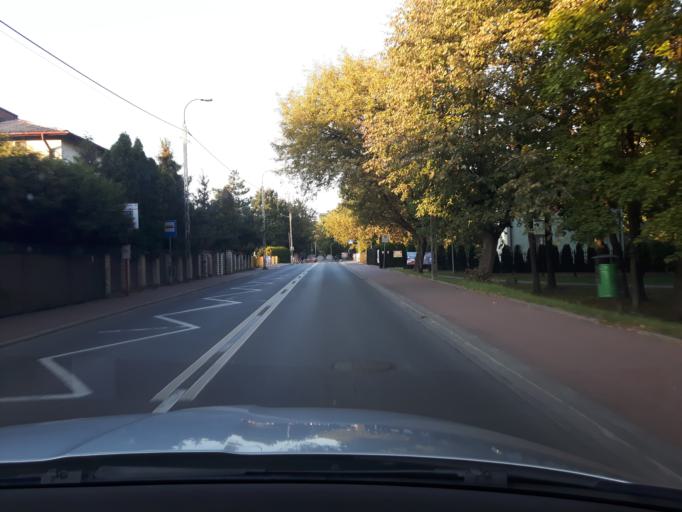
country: PL
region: Masovian Voivodeship
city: Zielonka
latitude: 52.3125
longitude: 21.1541
